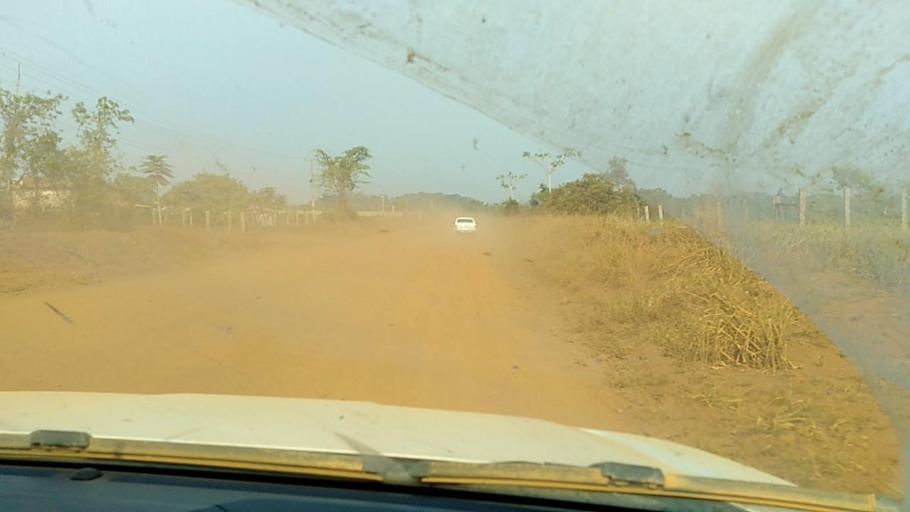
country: BR
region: Rondonia
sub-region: Porto Velho
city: Porto Velho
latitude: -8.7598
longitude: -63.9726
